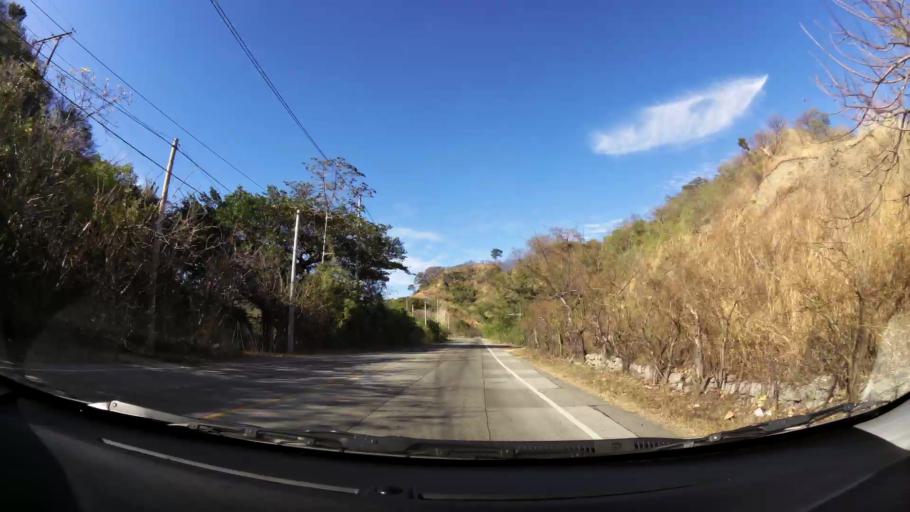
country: SV
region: Santa Ana
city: Texistepeque
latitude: 14.1448
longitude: -89.5143
